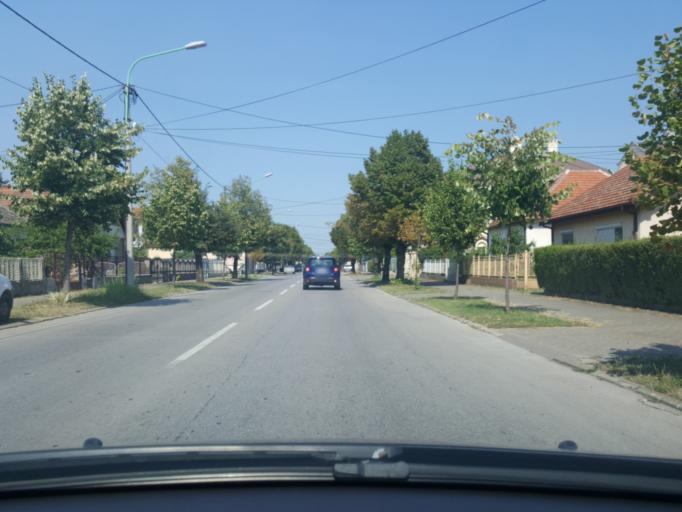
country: RS
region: Central Serbia
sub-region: Macvanski Okrug
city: Sabac
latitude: 44.7407
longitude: 19.6938
